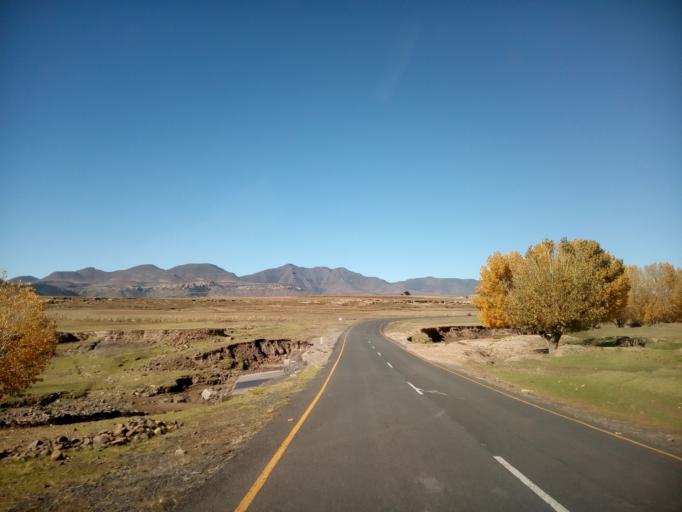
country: LS
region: Mafeteng
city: Mafeteng
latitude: -29.7282
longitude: 27.5011
